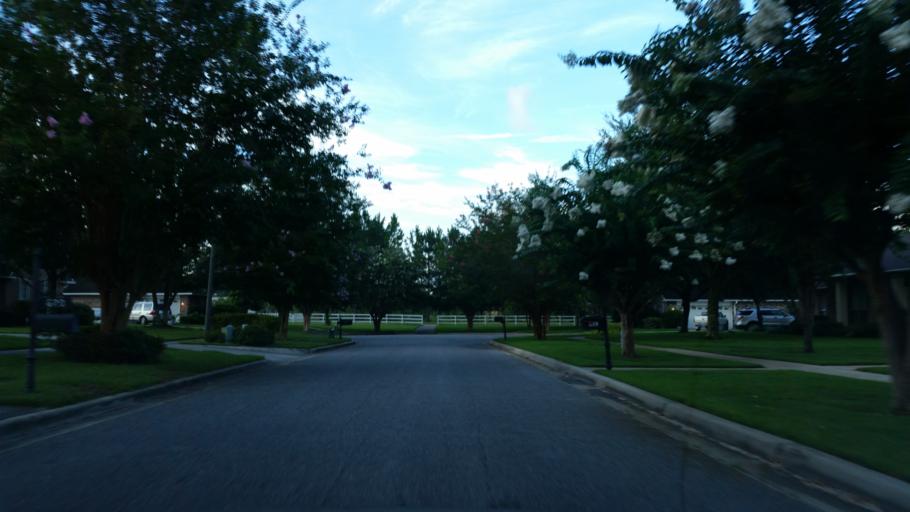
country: US
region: Florida
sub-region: Escambia County
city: Ensley
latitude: 30.5375
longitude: -87.3101
